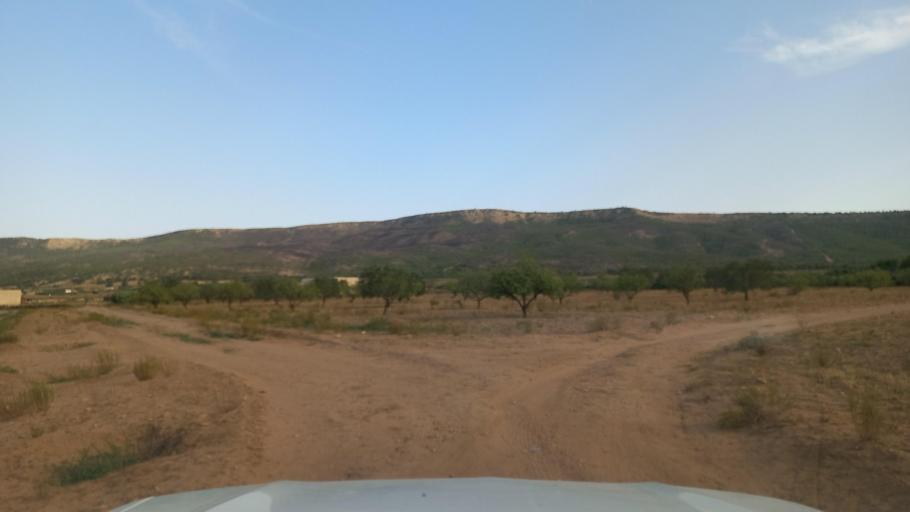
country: TN
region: Al Qasrayn
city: Kasserine
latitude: 35.3543
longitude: 8.8553
